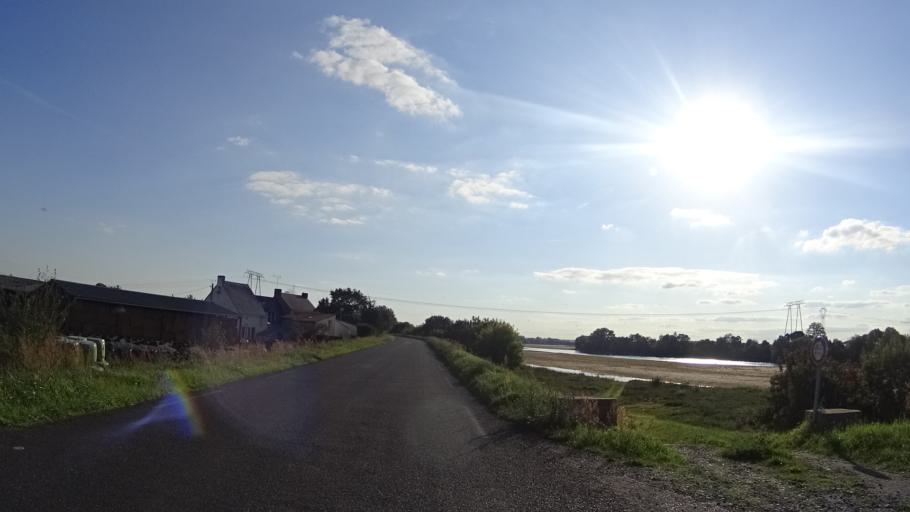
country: FR
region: Pays de la Loire
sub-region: Departement de Maine-et-Loire
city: Ingrandes
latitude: 47.3895
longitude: -0.9308
